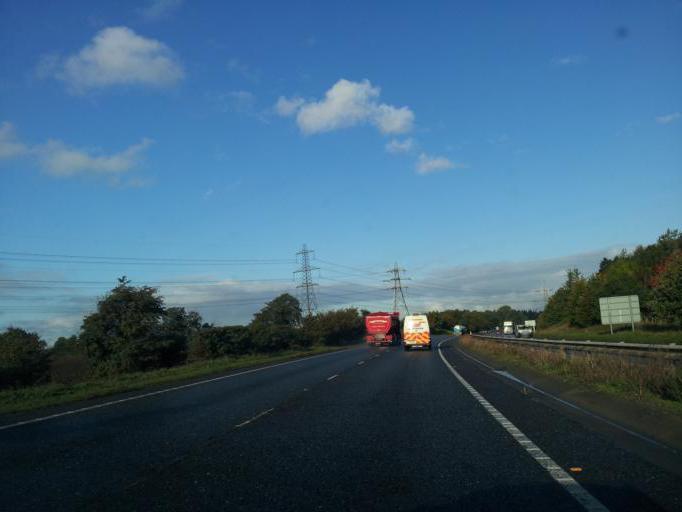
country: GB
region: England
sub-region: Norfolk
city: Cringleford
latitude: 52.5861
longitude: 1.2575
